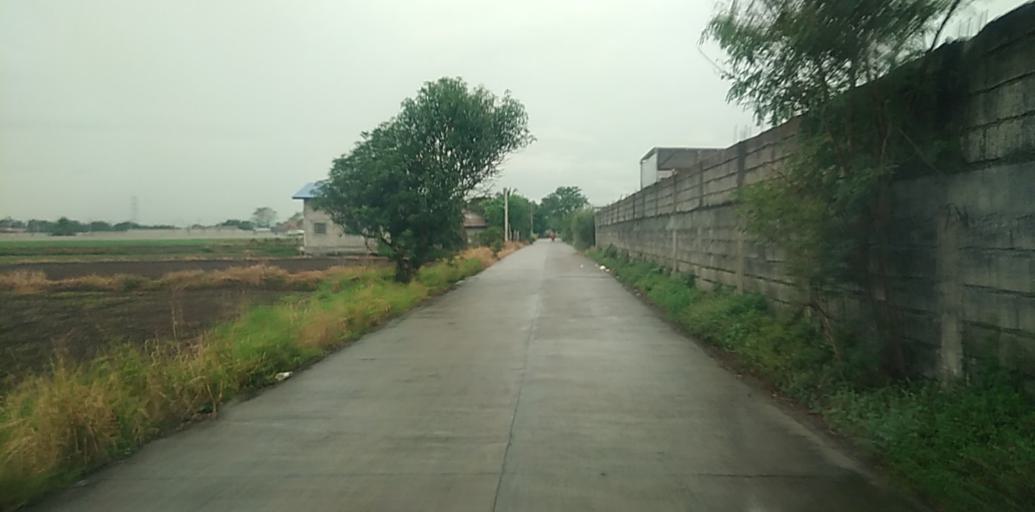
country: PH
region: Central Luzon
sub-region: Province of Pampanga
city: Anao
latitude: 15.1388
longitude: 120.6971
